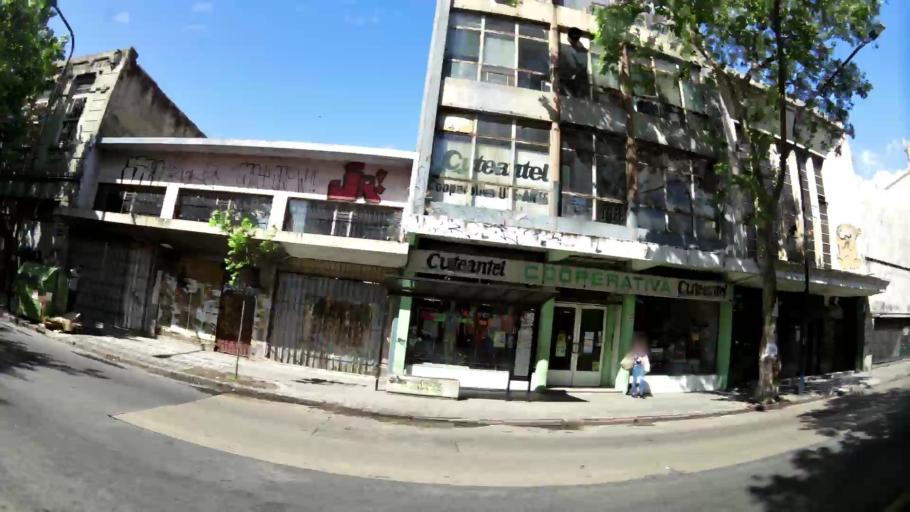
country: UY
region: Montevideo
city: Montevideo
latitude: -34.8886
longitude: -56.1880
